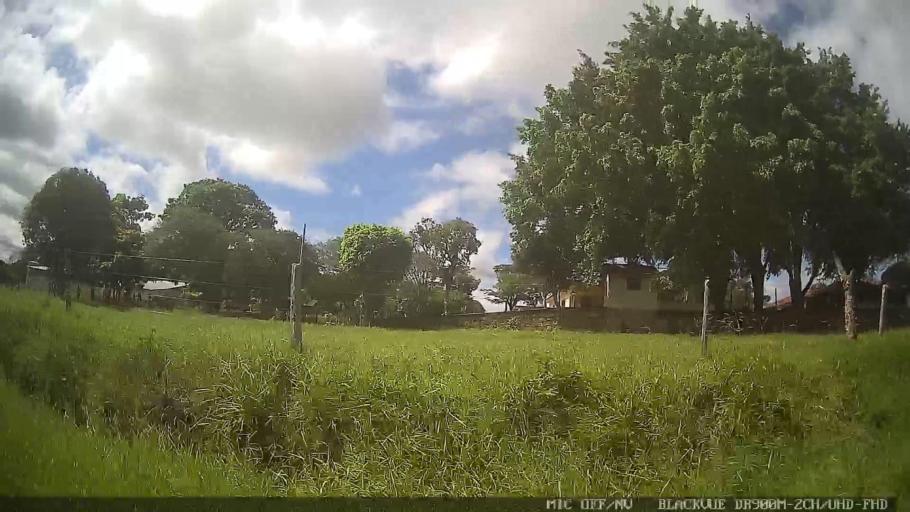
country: BR
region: Sao Paulo
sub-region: Amparo
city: Amparo
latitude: -22.8616
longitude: -46.7284
